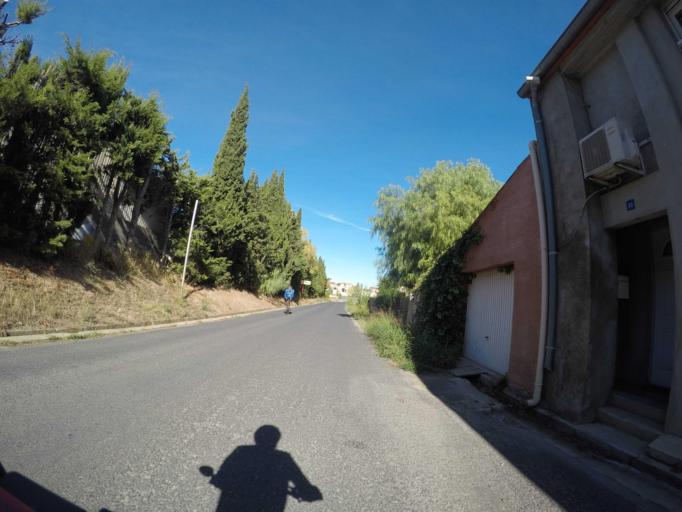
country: FR
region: Languedoc-Roussillon
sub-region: Departement des Pyrenees-Orientales
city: Ponteilla
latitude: 42.6278
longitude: 2.8125
